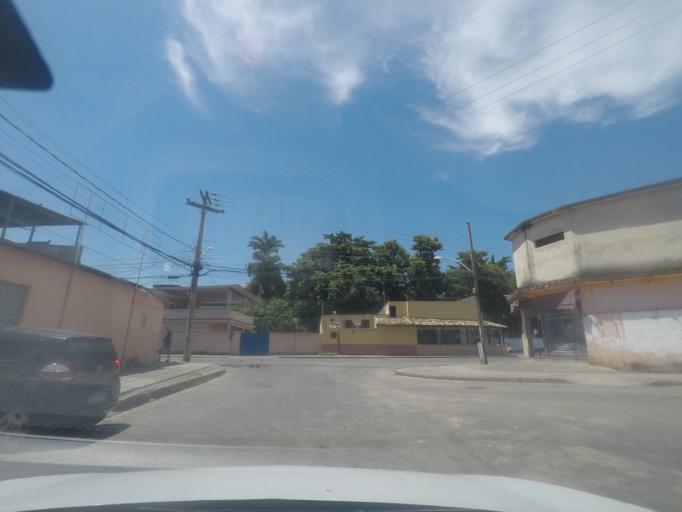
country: BR
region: Rio de Janeiro
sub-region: Itaguai
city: Itaguai
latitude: -23.0025
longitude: -43.6364
